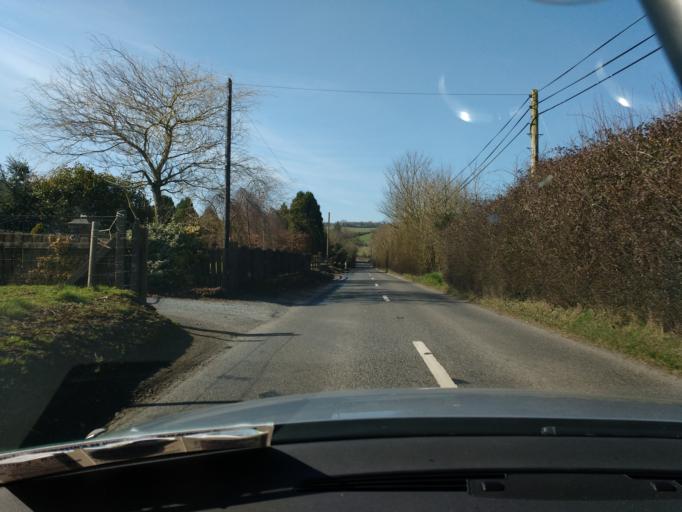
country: IE
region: Munster
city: Thurles
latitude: 52.6902
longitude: -7.9299
